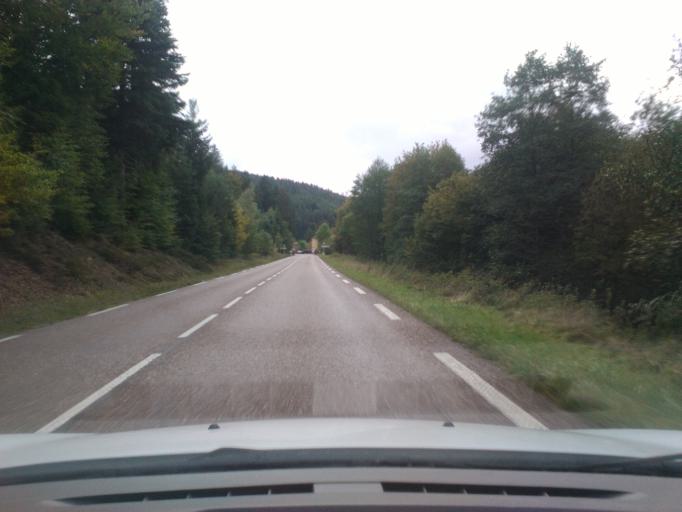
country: FR
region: Lorraine
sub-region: Departement des Vosges
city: Bruyeres
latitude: 48.2577
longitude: 6.7932
